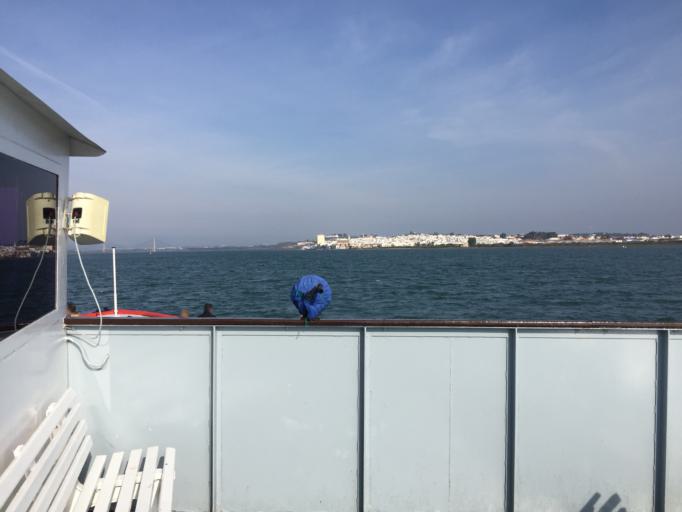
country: PT
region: Faro
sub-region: Vila Real de Santo Antonio
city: Vila Real de Santo Antonio
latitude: 37.1997
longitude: -7.4124
